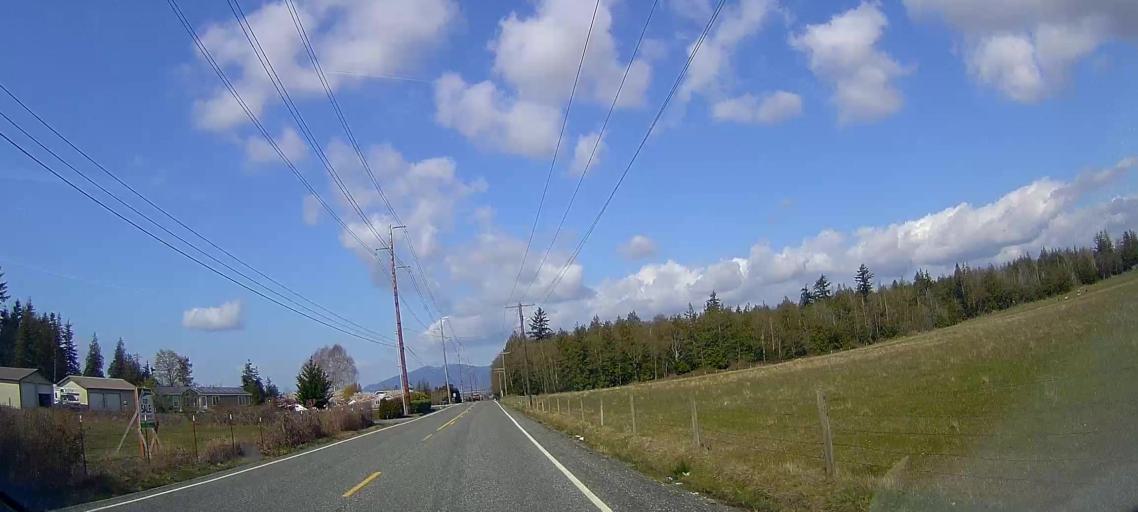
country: US
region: Washington
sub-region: Skagit County
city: Burlington
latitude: 48.4991
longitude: -122.4445
